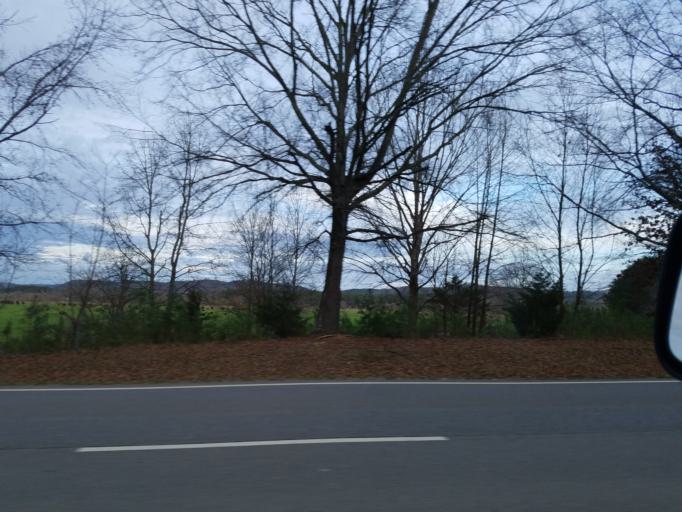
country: US
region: Georgia
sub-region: Bartow County
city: Rydal
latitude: 34.4439
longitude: -84.7236
